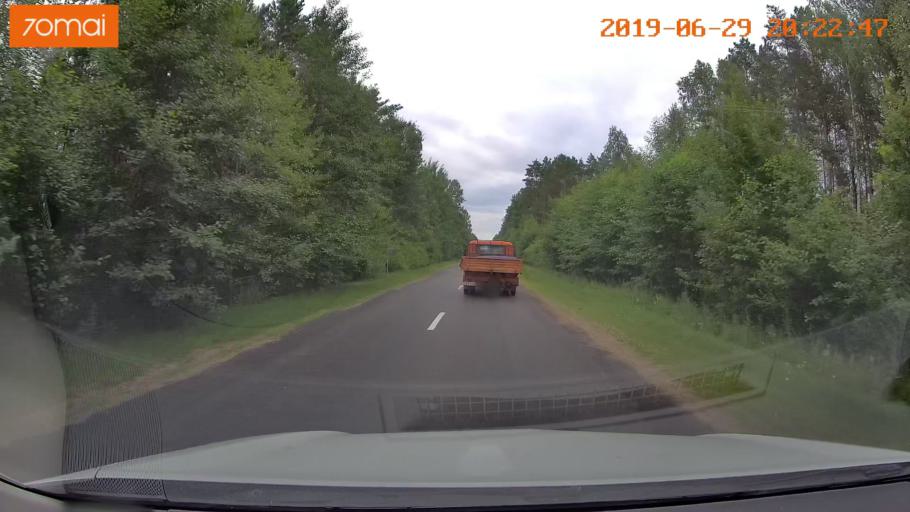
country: BY
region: Brest
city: Asnyezhytsy
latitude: 52.4364
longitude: 26.2567
